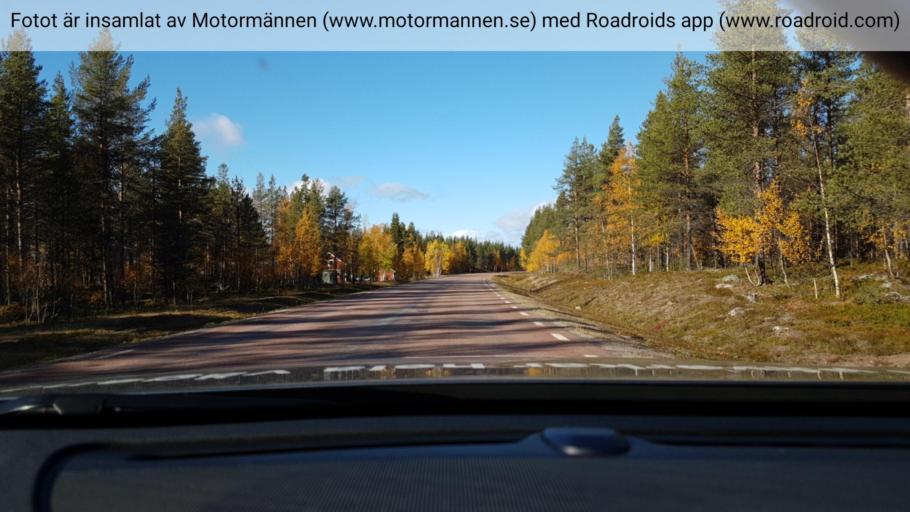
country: SE
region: Norrbotten
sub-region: Arjeplogs Kommun
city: Arjeplog
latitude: 66.0025
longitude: 18.1227
